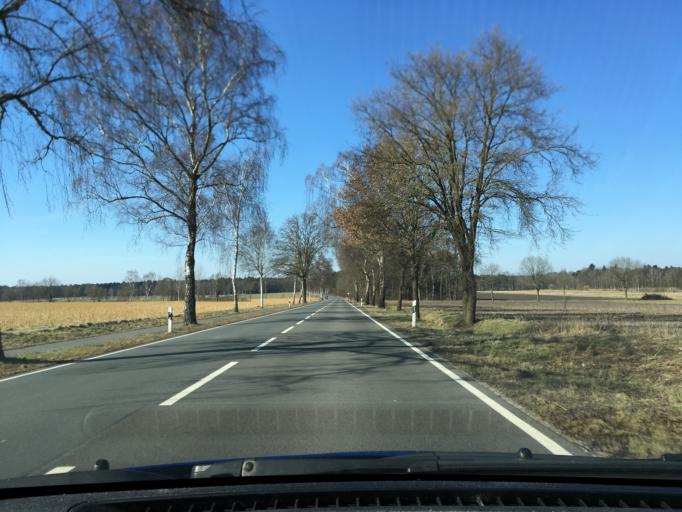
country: DE
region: Lower Saxony
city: Hemslingen
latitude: 53.0884
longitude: 9.5844
